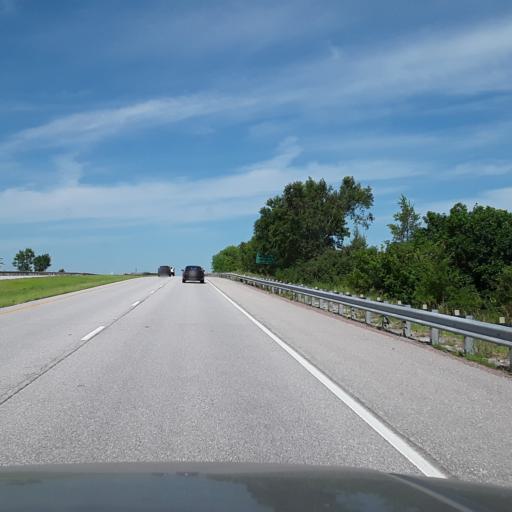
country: US
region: Nebraska
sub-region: Lancaster County
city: Lincoln
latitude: 40.8796
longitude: -96.7560
